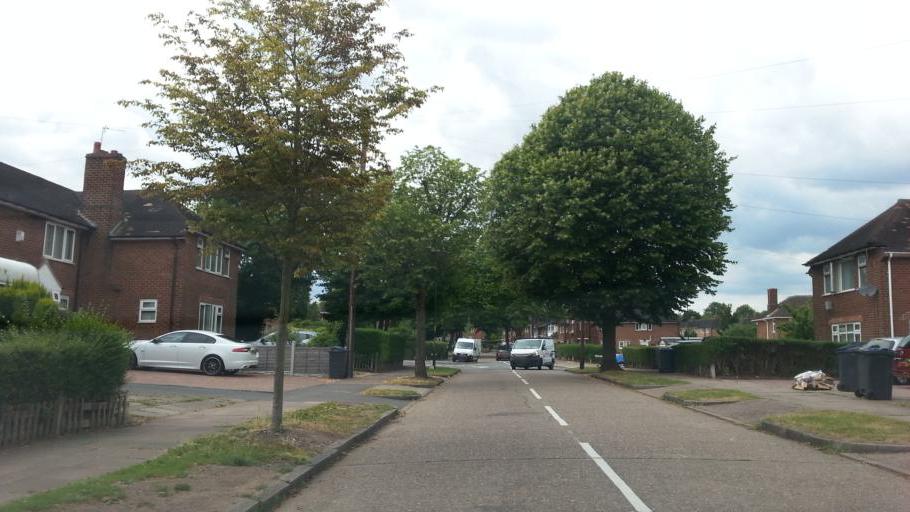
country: GB
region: England
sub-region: City and Borough of Birmingham
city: Acocks Green
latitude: 52.4768
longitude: -1.7963
